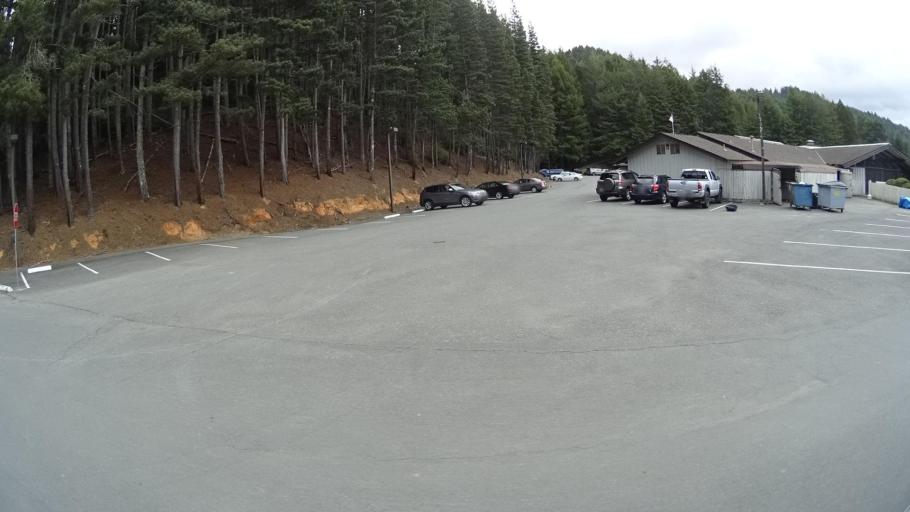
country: US
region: California
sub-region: Humboldt County
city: Bayside
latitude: 40.8471
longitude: -124.0486
